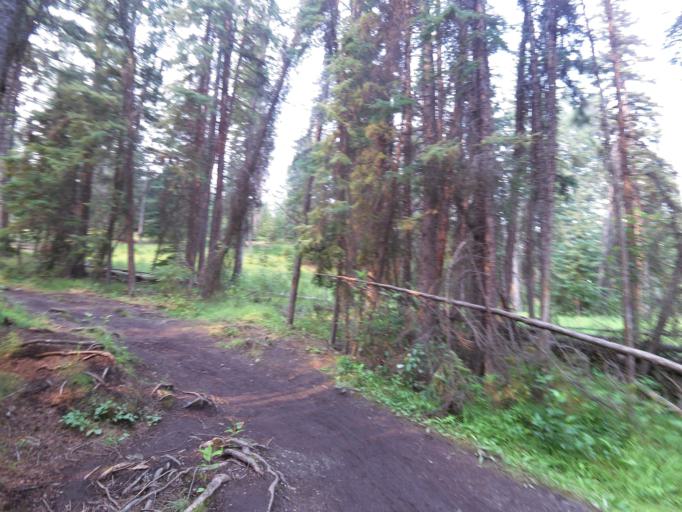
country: CA
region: Alberta
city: Jasper Park Lodge
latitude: 52.8845
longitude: -118.0643
